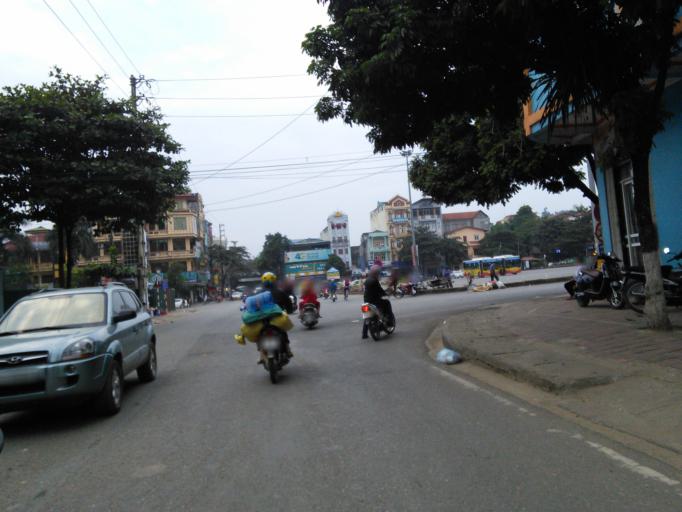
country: VN
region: Lao Cai
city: Lao Cai
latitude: 22.4911
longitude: 103.9779
